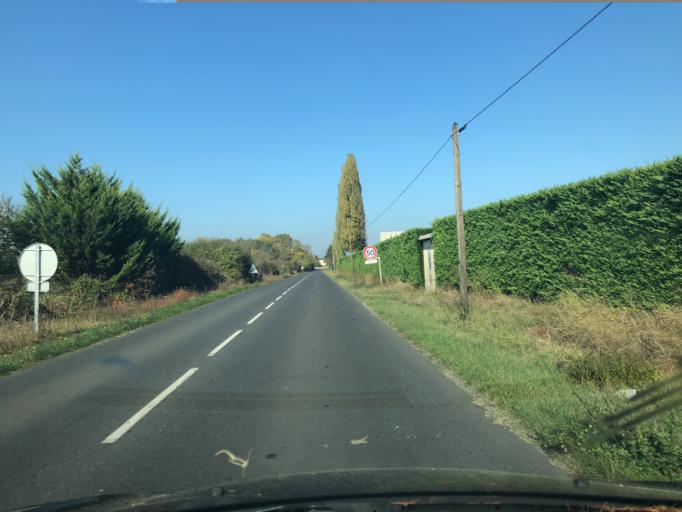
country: FR
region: Centre
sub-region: Departement d'Indre-et-Loire
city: Mettray
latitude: 47.4521
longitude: 0.6746
